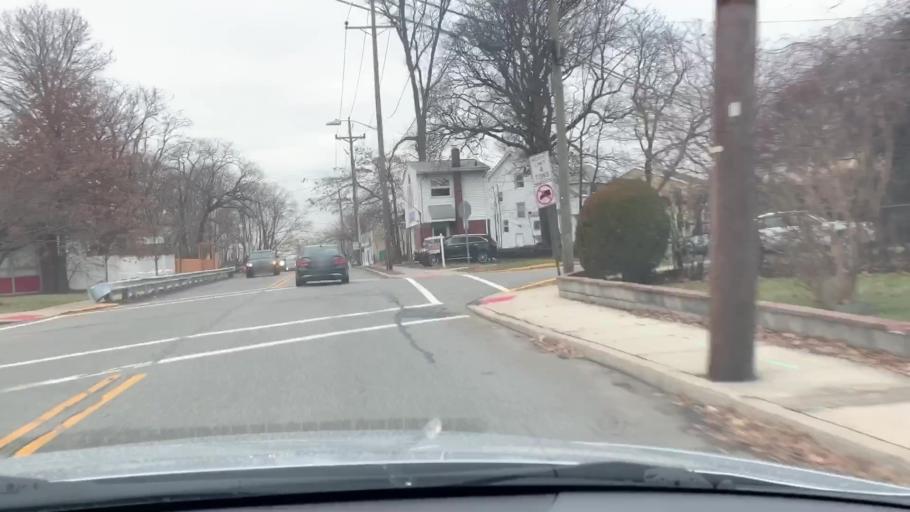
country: US
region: New Jersey
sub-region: Bergen County
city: Palisades Park
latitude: 40.8402
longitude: -74.0015
